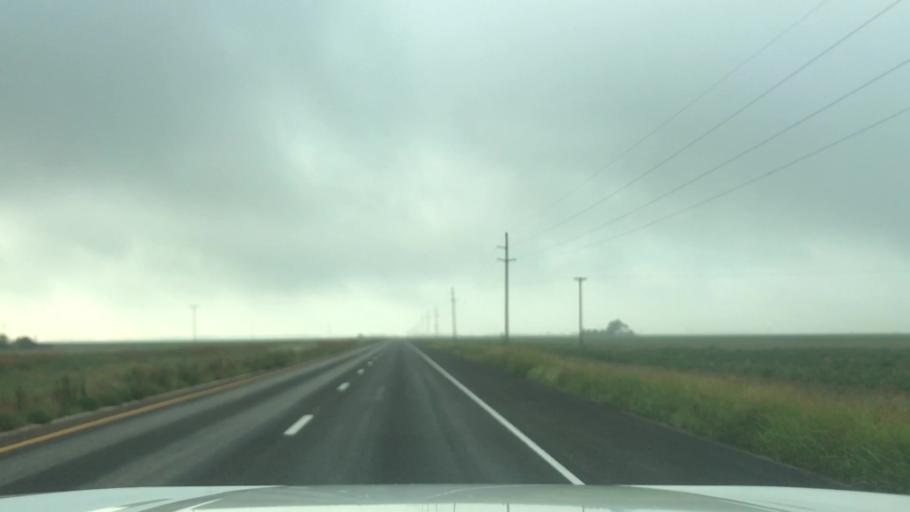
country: US
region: Texas
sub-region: Lubbock County
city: Slaton
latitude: 33.3753
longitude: -101.5783
